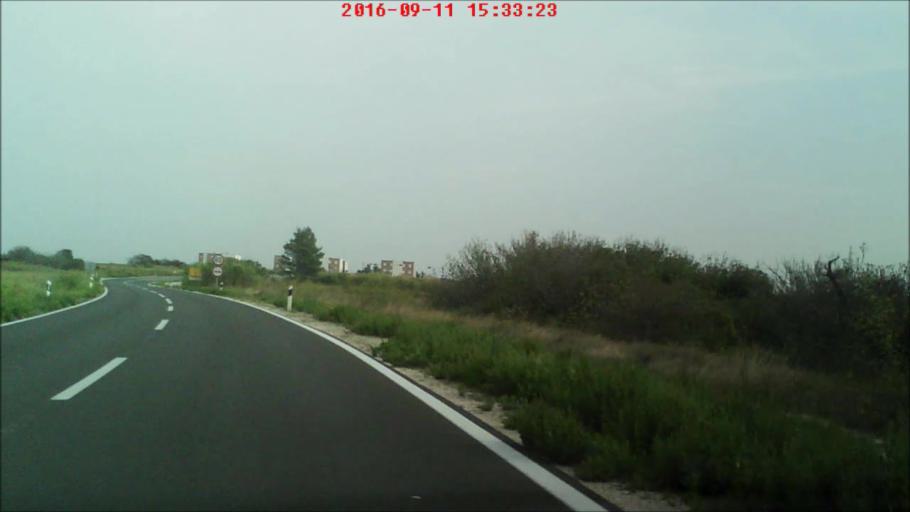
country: HR
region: Zadarska
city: Nin
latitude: 44.2478
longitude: 15.1649
